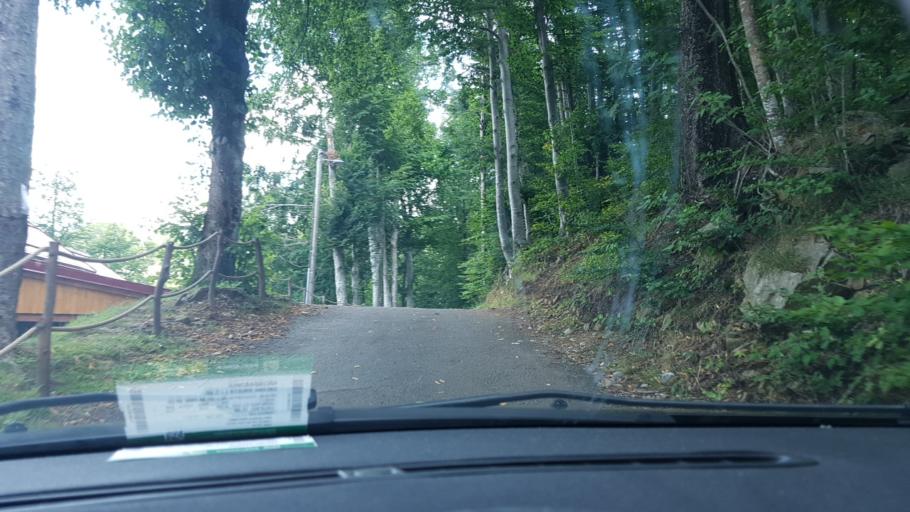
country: HR
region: Primorsko-Goranska
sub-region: Grad Delnice
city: Delnice
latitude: 45.3611
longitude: 14.7194
